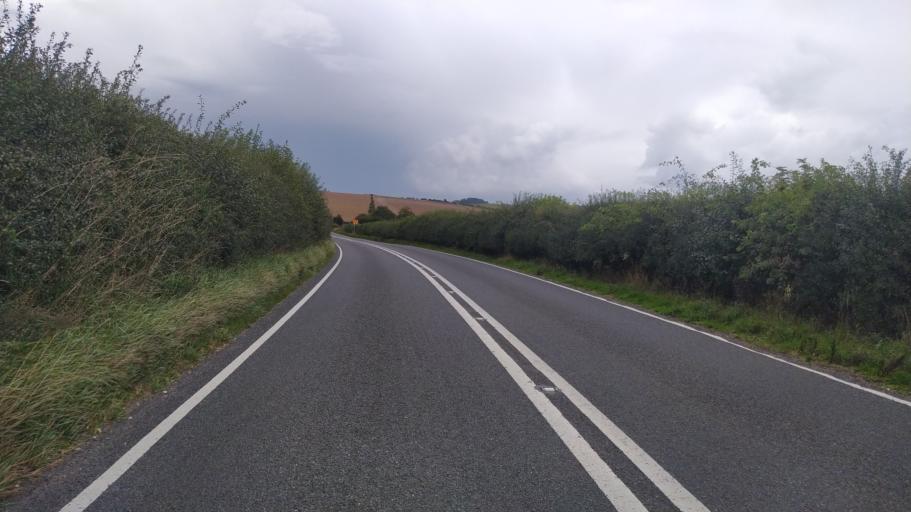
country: GB
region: England
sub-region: Wiltshire
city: Bower Chalke
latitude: 50.9372
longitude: -2.0031
